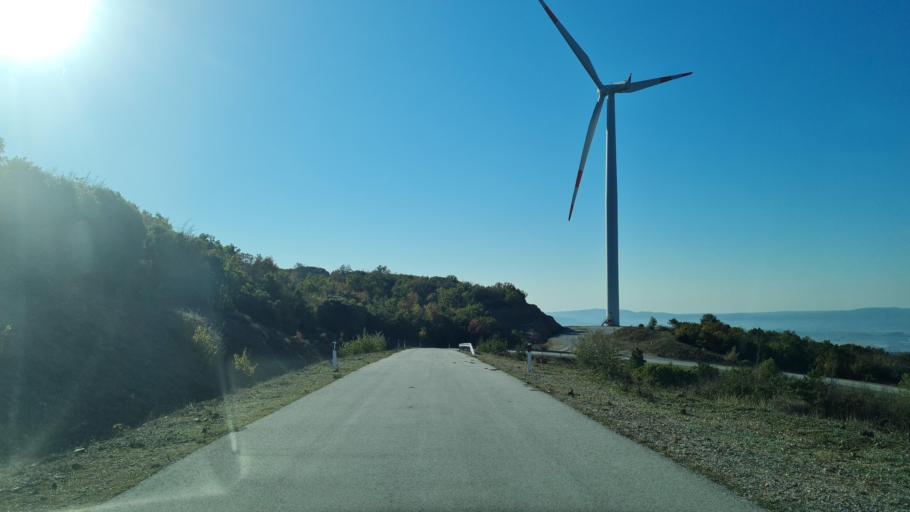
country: MK
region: Bogdanci
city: Bogdanci
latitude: 41.2246
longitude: 22.5536
